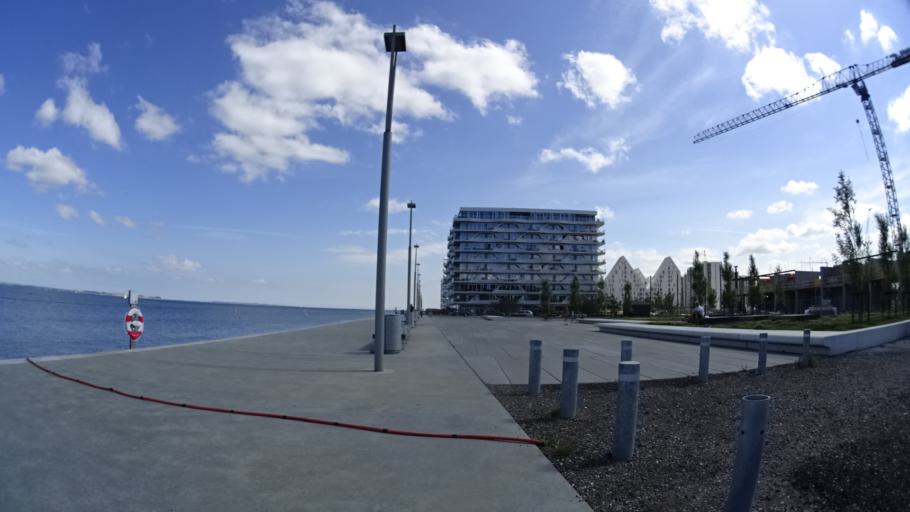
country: DK
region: Central Jutland
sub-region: Arhus Kommune
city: Arhus
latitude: 56.1680
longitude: 10.2276
